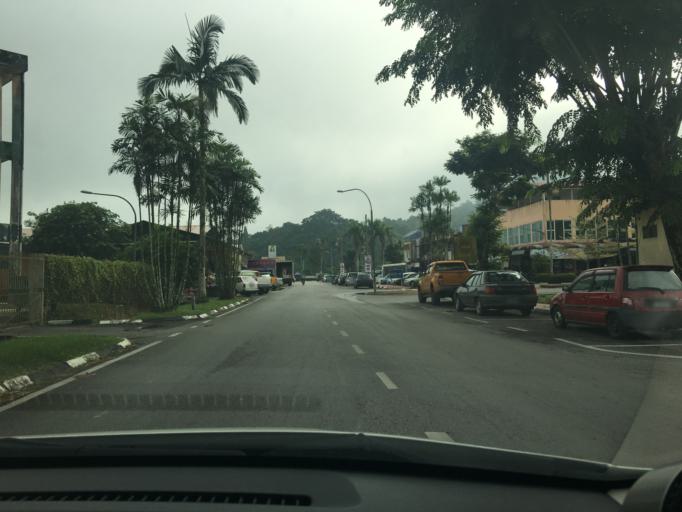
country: MY
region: Sarawak
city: Kuching
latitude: 1.4179
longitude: 110.1545
